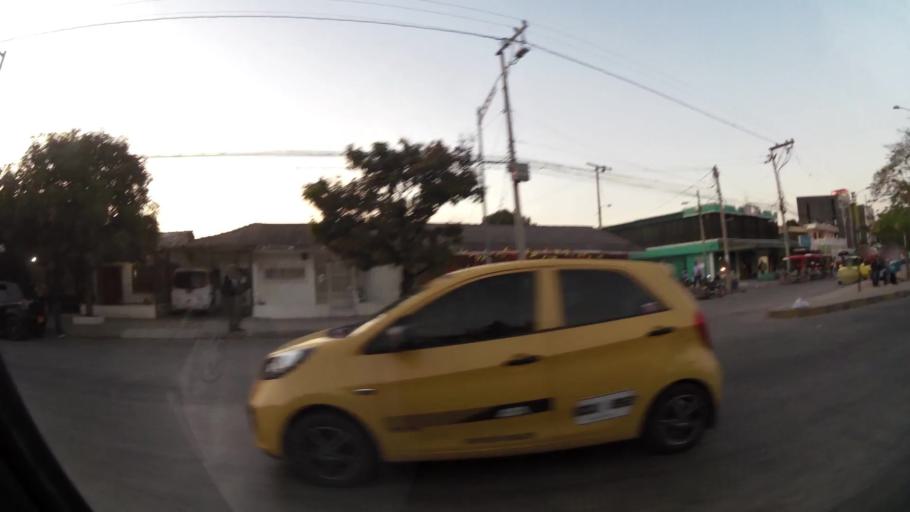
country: CO
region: Atlantico
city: Barranquilla
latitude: 10.9491
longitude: -74.7749
